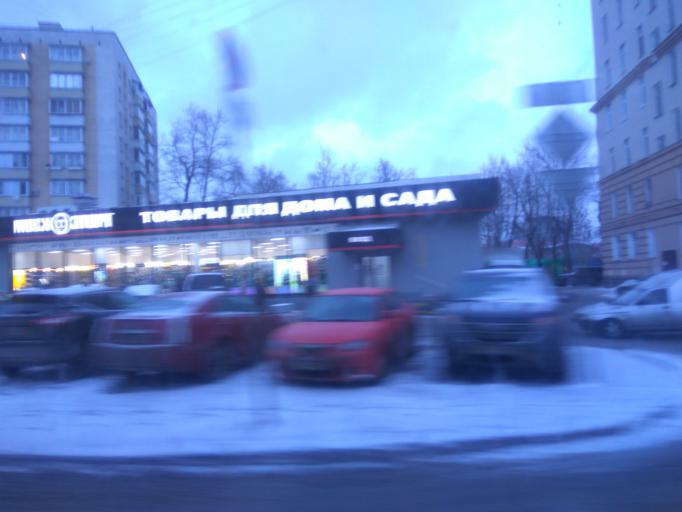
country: RU
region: Moscow
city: Taganskiy
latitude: 55.7288
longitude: 37.6778
